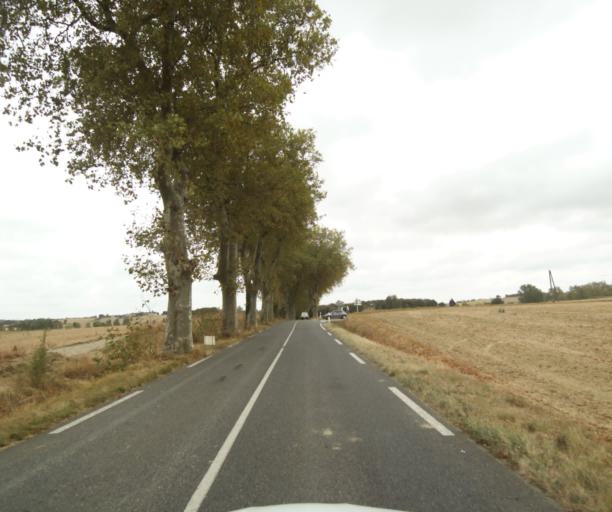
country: FR
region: Midi-Pyrenees
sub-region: Departement de la Haute-Garonne
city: Villefranche-de-Lauragais
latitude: 43.4127
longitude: 1.7376
